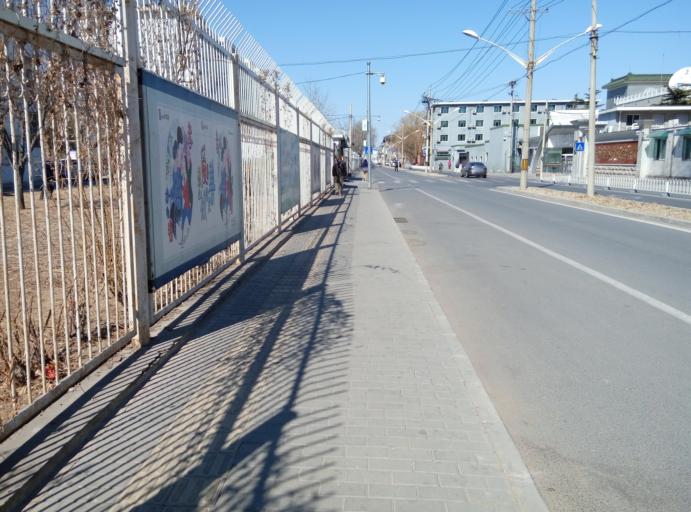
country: CN
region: Beijing
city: Haidian
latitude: 39.9897
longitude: 116.2866
